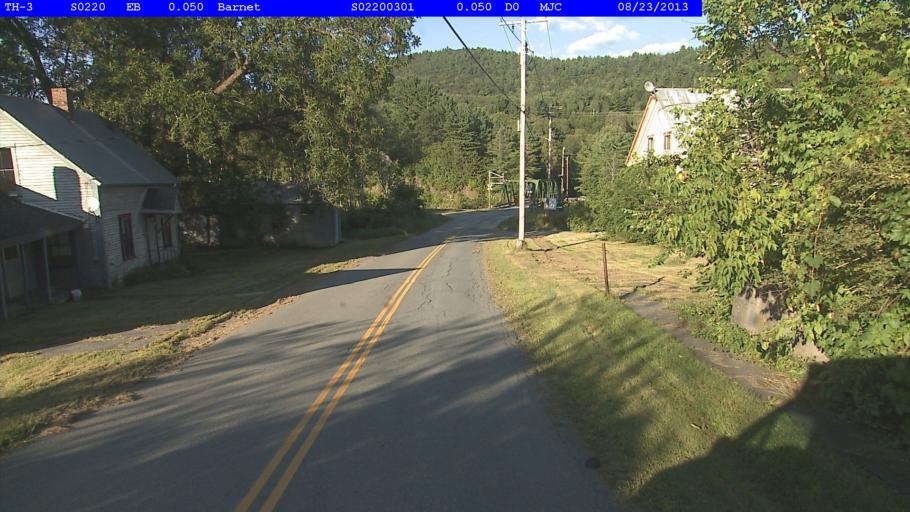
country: US
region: Vermont
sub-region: Caledonia County
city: Saint Johnsbury
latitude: 44.3268
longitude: -72.0376
